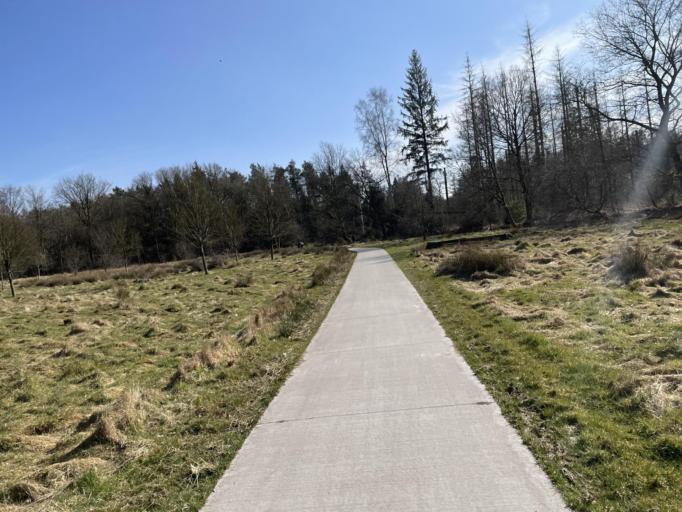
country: NL
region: Drenthe
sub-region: Gemeente Westerveld
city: Dwingeloo
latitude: 52.9059
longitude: 6.3612
